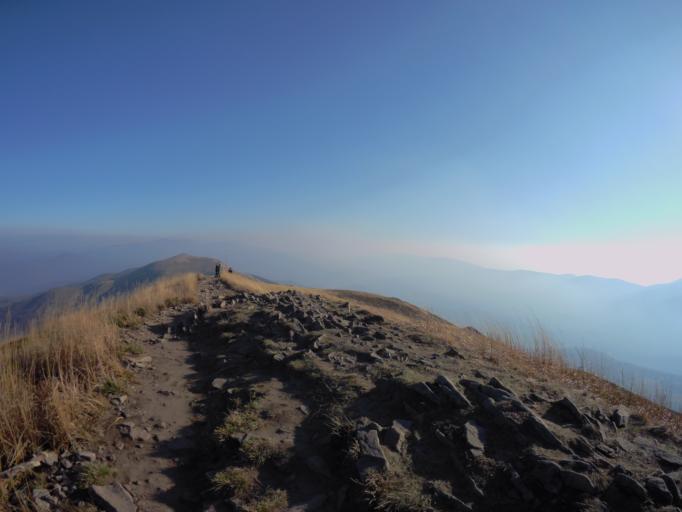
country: PL
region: Subcarpathian Voivodeship
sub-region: Powiat bieszczadzki
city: Lutowiska
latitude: 49.1381
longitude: 22.6035
